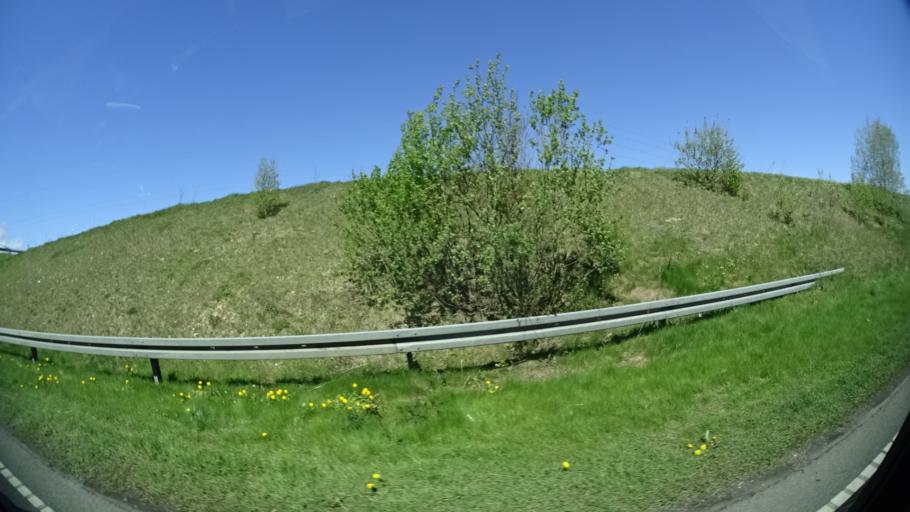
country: DK
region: Central Jutland
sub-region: Arhus Kommune
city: Kolt
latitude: 56.1214
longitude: 10.0671
